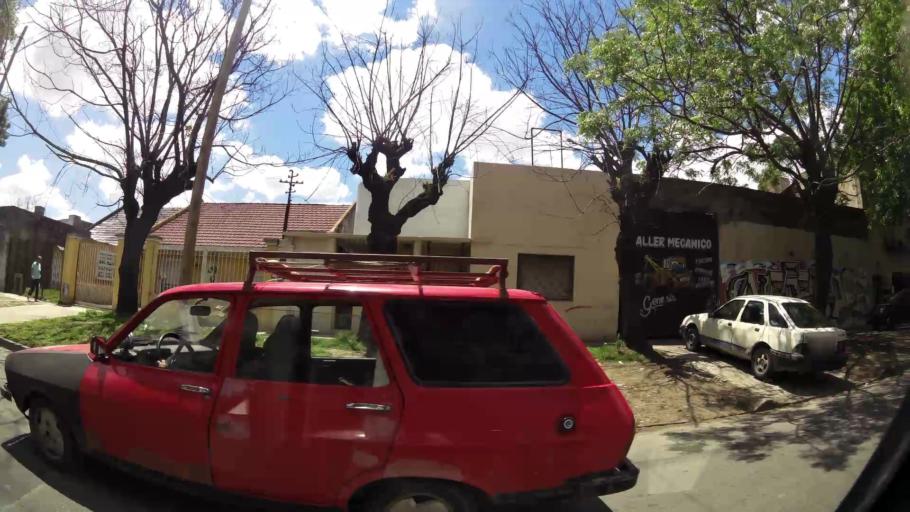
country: AR
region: Buenos Aires
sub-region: Partido de Lanus
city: Lanus
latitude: -34.6997
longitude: -58.4293
